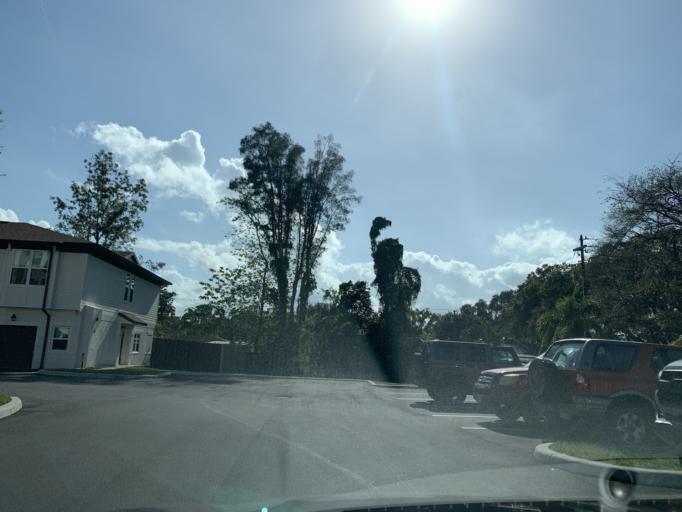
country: US
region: Florida
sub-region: Hillsborough County
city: Tampa
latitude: 27.8884
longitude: -82.5115
